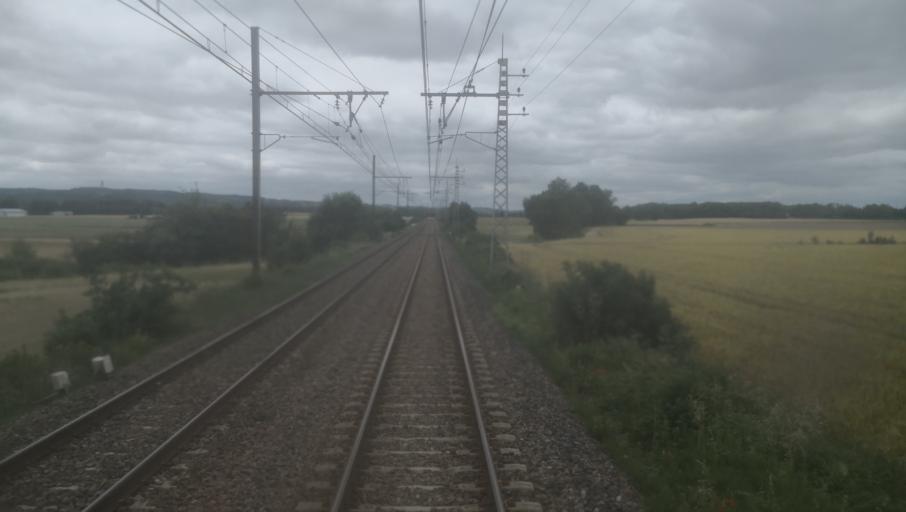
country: FR
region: Languedoc-Roussillon
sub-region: Departement de l'Aude
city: Castelnaudary
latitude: 43.3138
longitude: 1.9294
